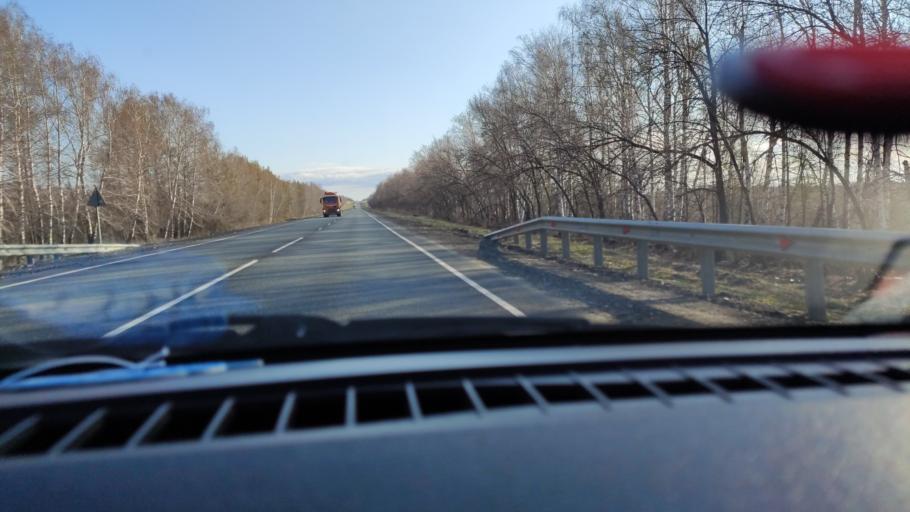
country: RU
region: Saratov
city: Khvalynsk
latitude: 52.5765
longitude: 48.1104
